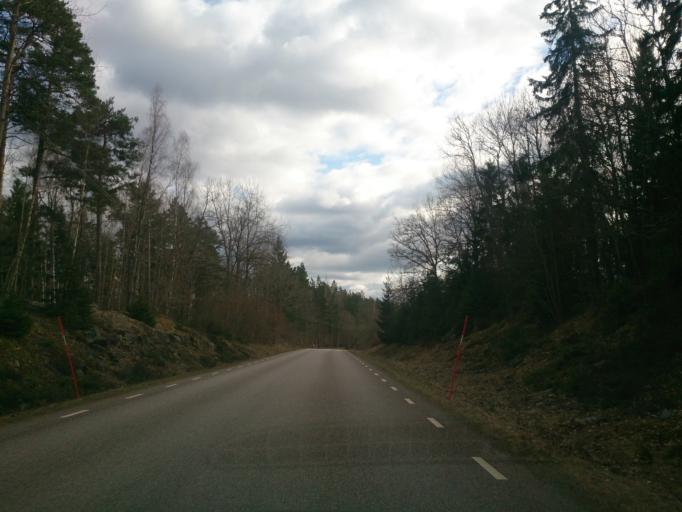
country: SE
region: OEstergoetland
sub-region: Atvidabergs Kommun
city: Atvidaberg
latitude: 58.3200
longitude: 16.0270
